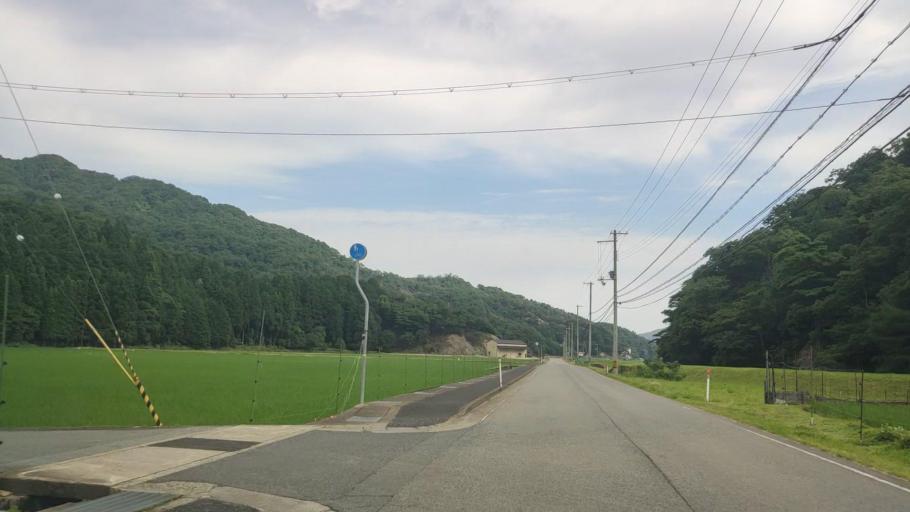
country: JP
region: Hyogo
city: Toyooka
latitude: 35.6177
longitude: 134.8429
